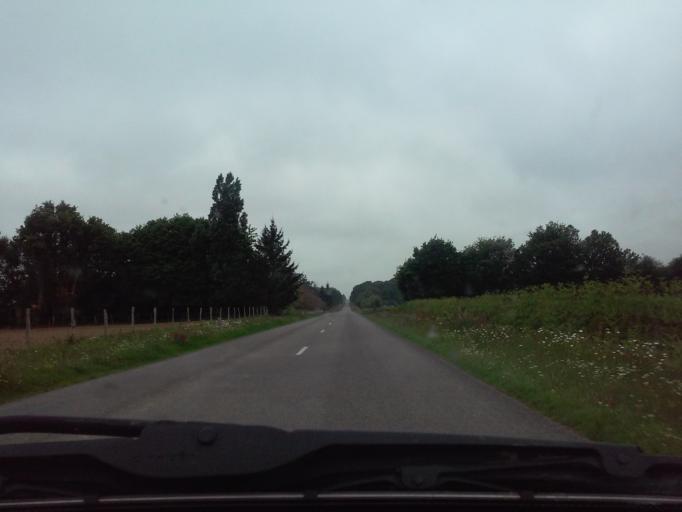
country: FR
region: Pays de la Loire
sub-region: Departement de la Mayenne
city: Ballots
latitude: 47.9619
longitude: -1.0013
